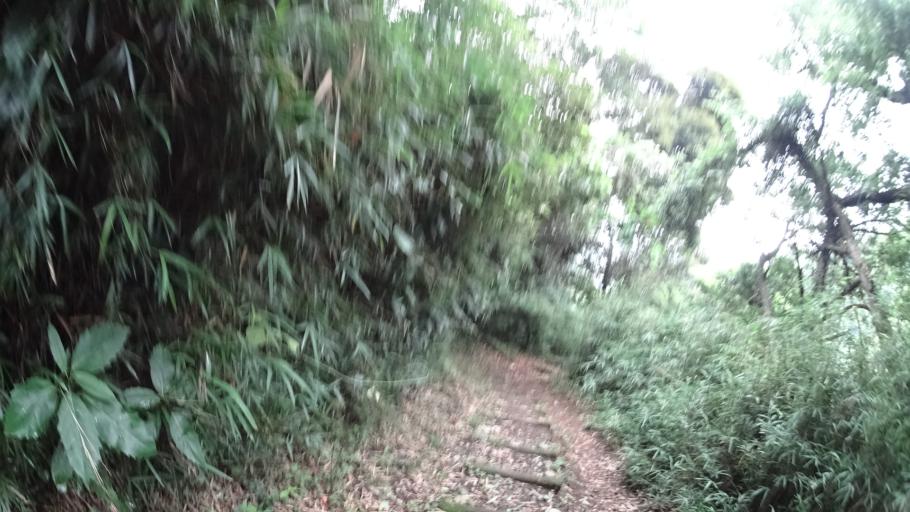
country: JP
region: Kanagawa
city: Yokosuka
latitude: 35.2484
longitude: 139.6558
